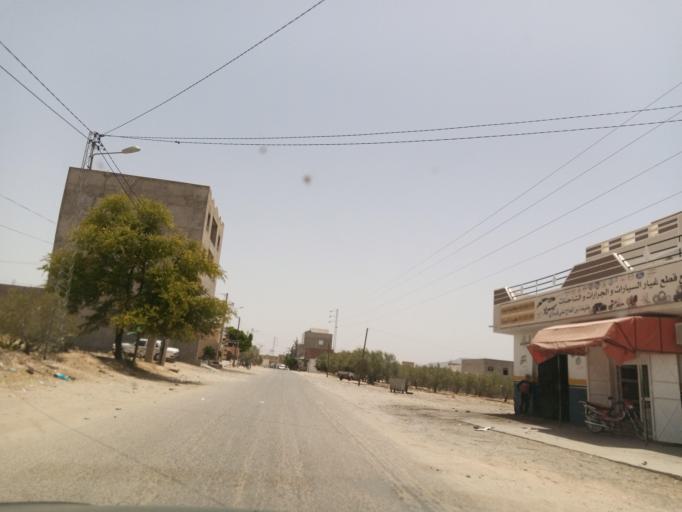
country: TN
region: Al Qasrayn
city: Kasserine
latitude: 35.2144
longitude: 8.8929
